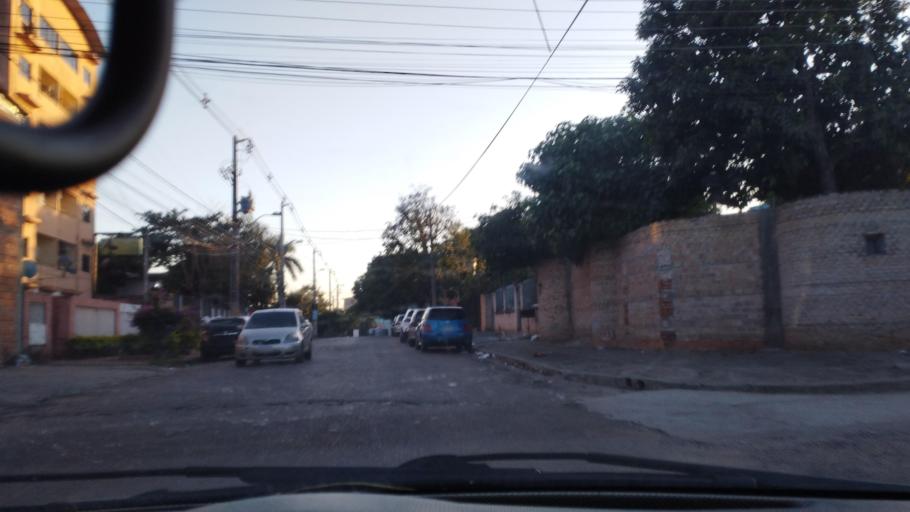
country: PY
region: Central
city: Fernando de la Mora
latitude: -25.3051
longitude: -57.5334
